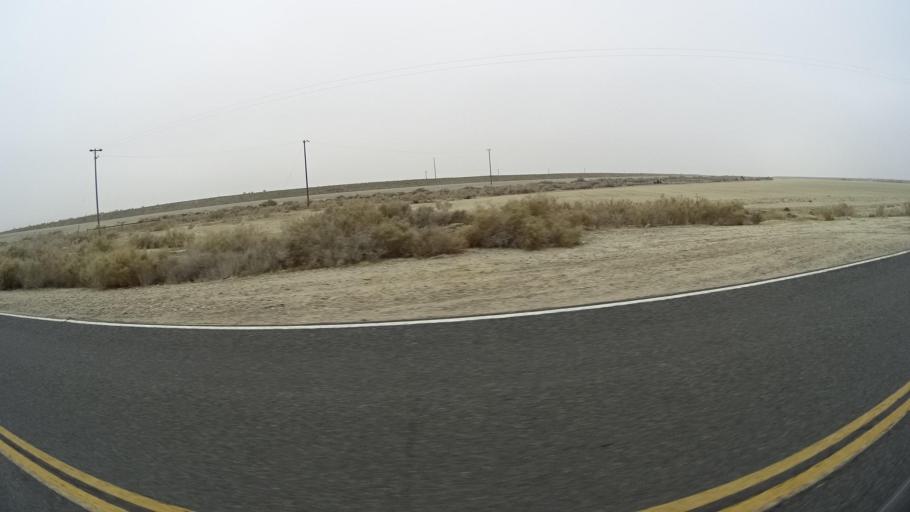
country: US
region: California
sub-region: Kern County
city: Buttonwillow
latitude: 35.3554
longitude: -119.4741
